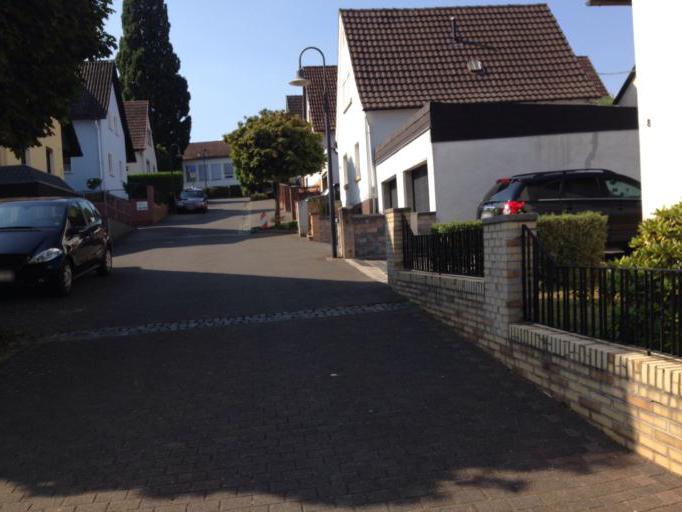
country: DE
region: Hesse
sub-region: Regierungsbezirk Giessen
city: Giessen
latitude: 50.6220
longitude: 8.6570
